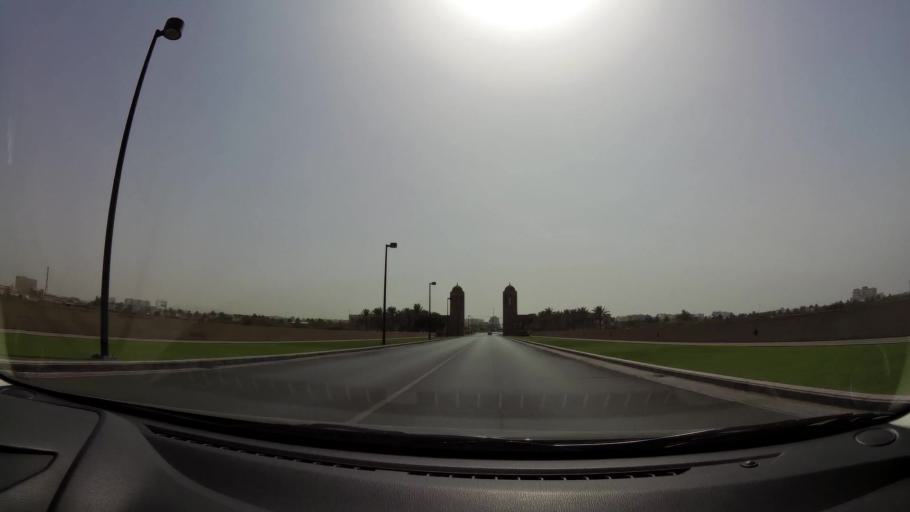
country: OM
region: Muhafazat Masqat
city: Bawshar
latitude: 23.5820
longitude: 58.3856
